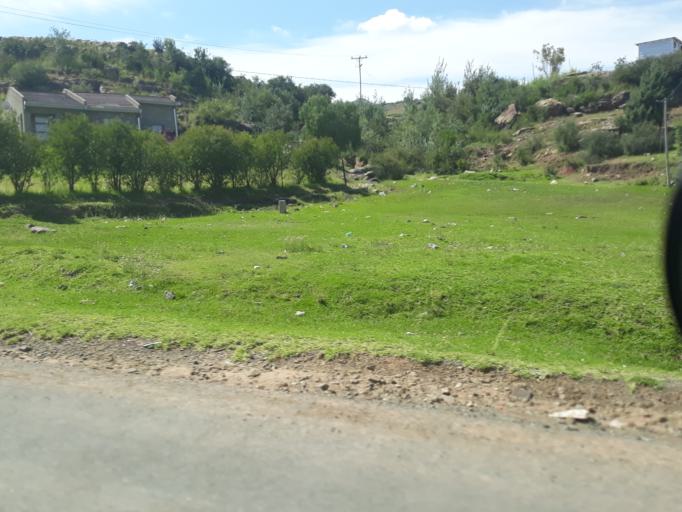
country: LS
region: Mohale's Hoek District
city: Mohale's Hoek
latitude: -30.1038
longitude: 27.4772
